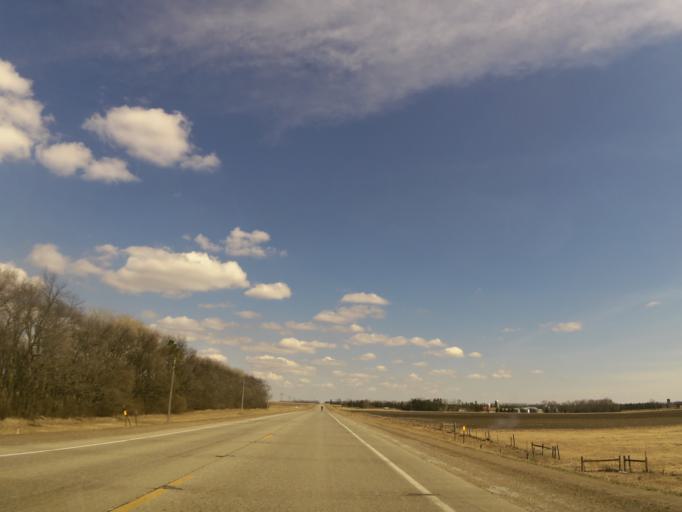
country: US
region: South Dakota
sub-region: Codington County
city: Watertown
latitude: 44.8901
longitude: -97.0145
